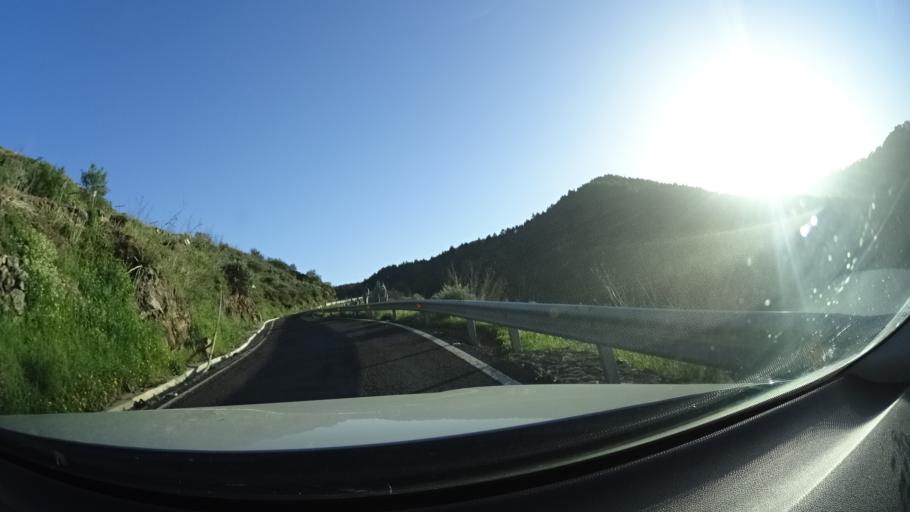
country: ES
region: Canary Islands
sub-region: Provincia de Las Palmas
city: Artenara
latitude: 28.0366
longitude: -15.6717
